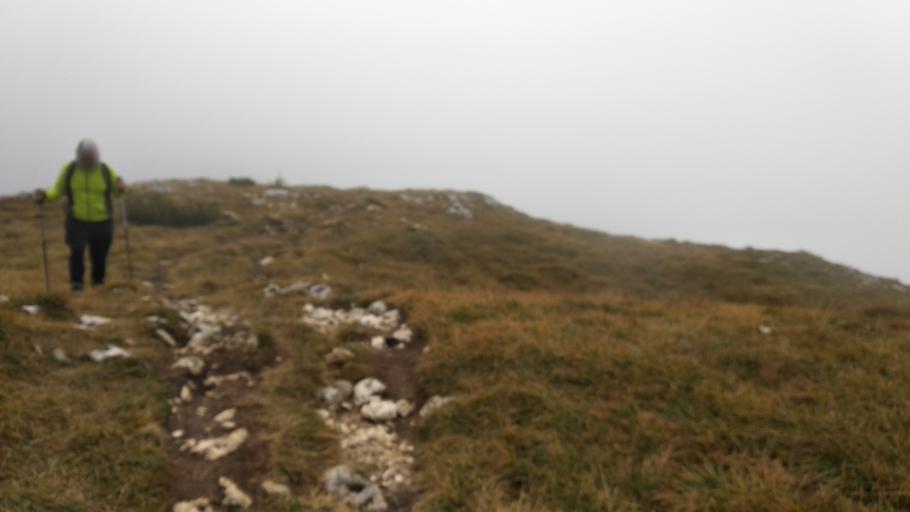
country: IT
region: Trentino-Alto Adige
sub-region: Provincia di Trento
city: Borgo
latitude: 45.9711
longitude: 11.4467
